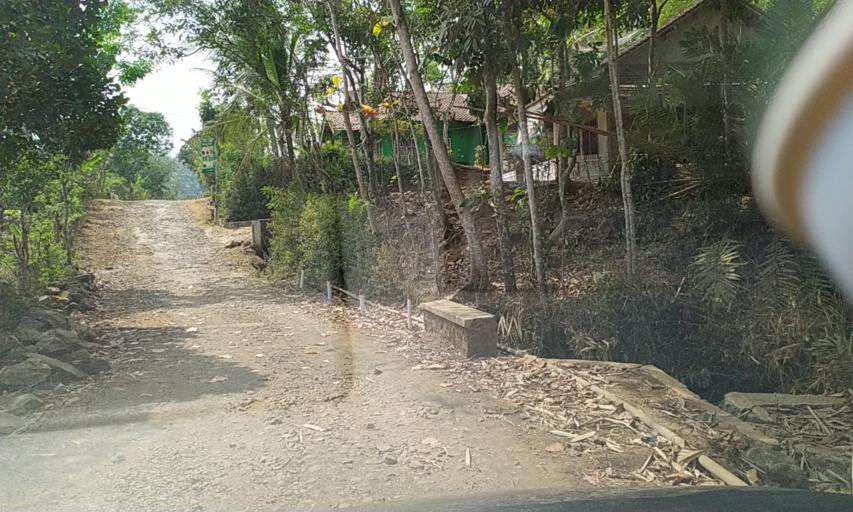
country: ID
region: Central Java
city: Gunungwilis
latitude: -7.4219
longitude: 108.7985
